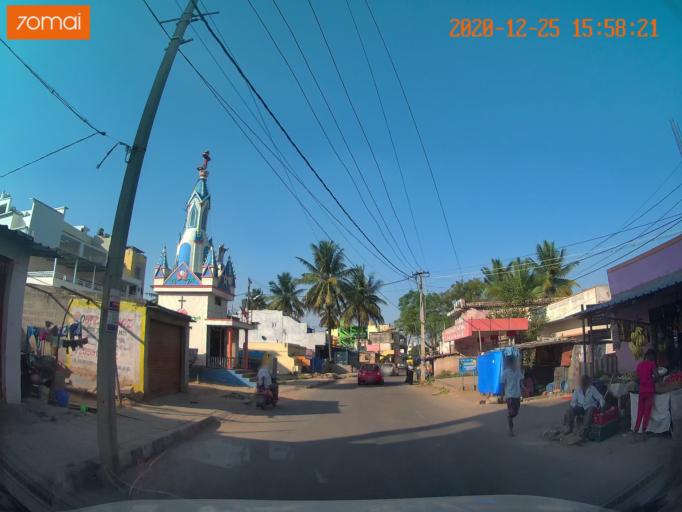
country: IN
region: Karnataka
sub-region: Bangalore Urban
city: Bangalore
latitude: 12.8712
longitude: 77.6244
